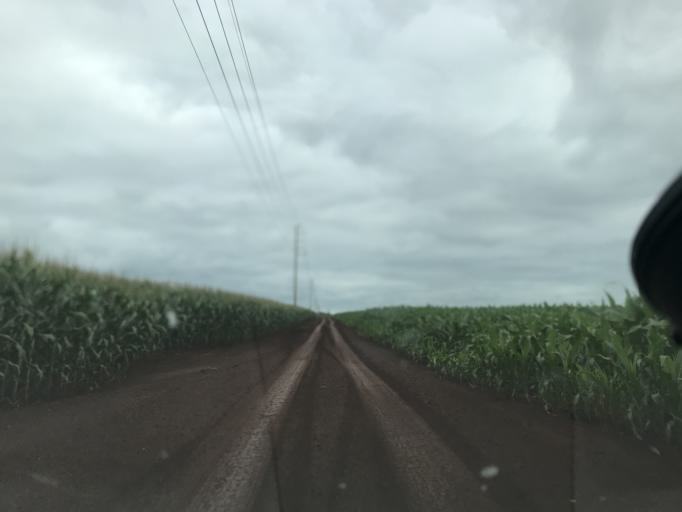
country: BR
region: Parana
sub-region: Palotina
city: Palotina
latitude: -24.3021
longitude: -53.8195
